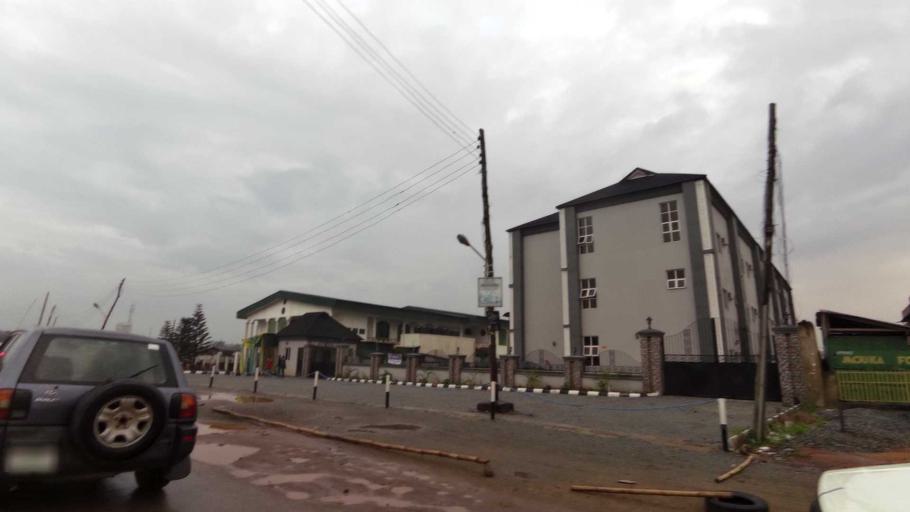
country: NG
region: Oyo
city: Ibadan
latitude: 7.4309
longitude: 3.9407
